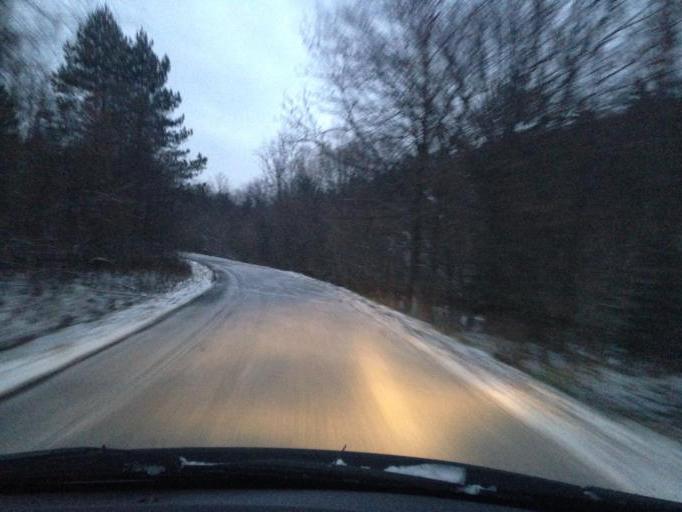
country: PL
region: Subcarpathian Voivodeship
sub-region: Powiat jasielski
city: Krempna
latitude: 49.5131
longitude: 21.5421
